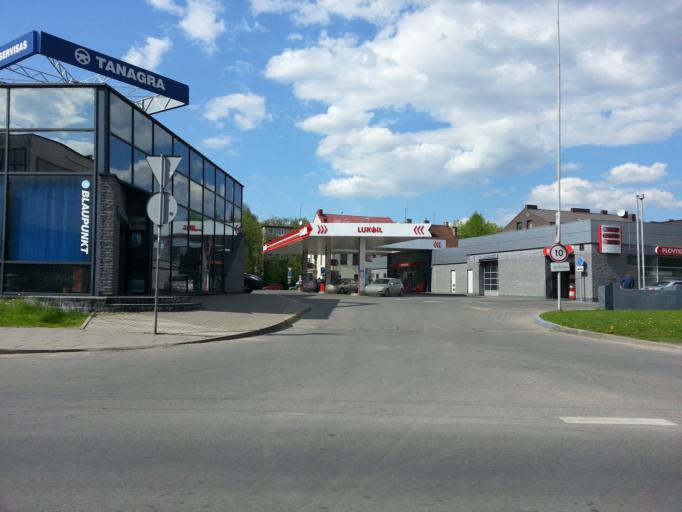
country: LT
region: Vilnius County
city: Naujamiestis
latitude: 54.6706
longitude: 25.2627
